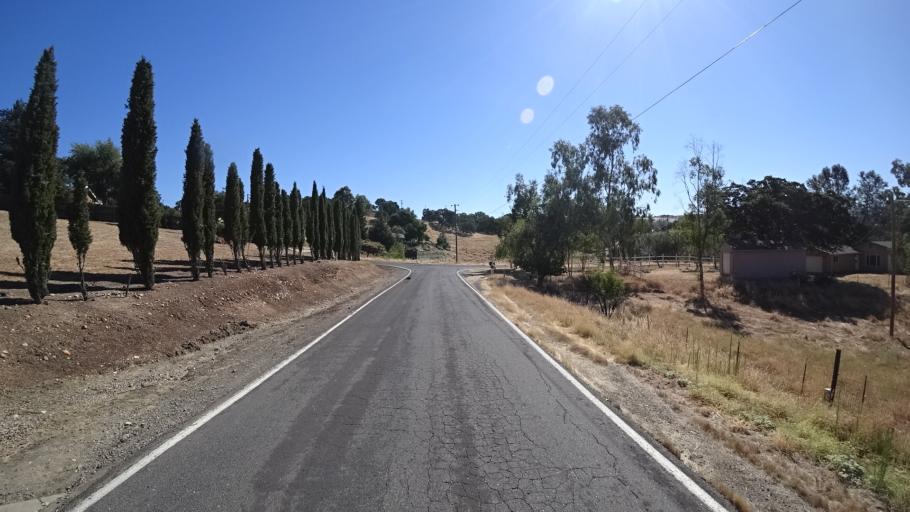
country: US
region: California
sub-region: Calaveras County
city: Rancho Calaveras
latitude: 38.0935
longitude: -120.8590
